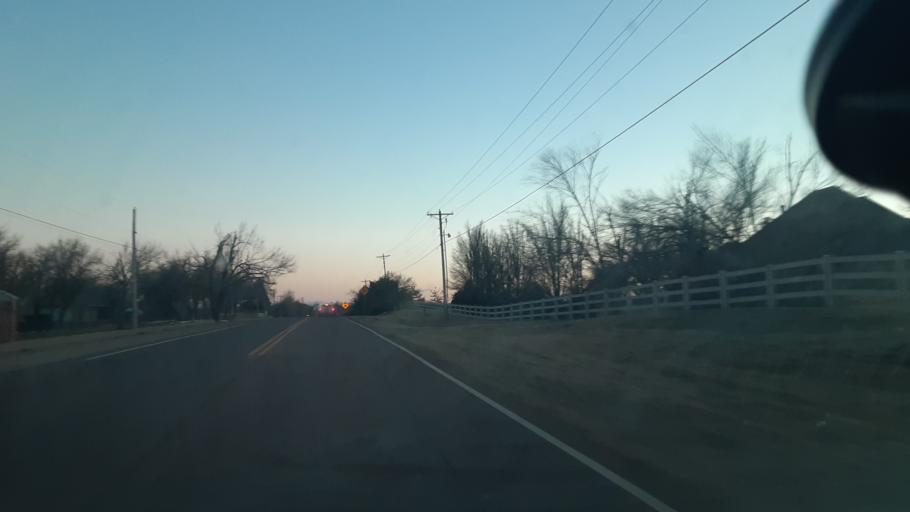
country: US
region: Oklahoma
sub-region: Oklahoma County
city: Edmond
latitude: 35.7136
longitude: -97.4252
